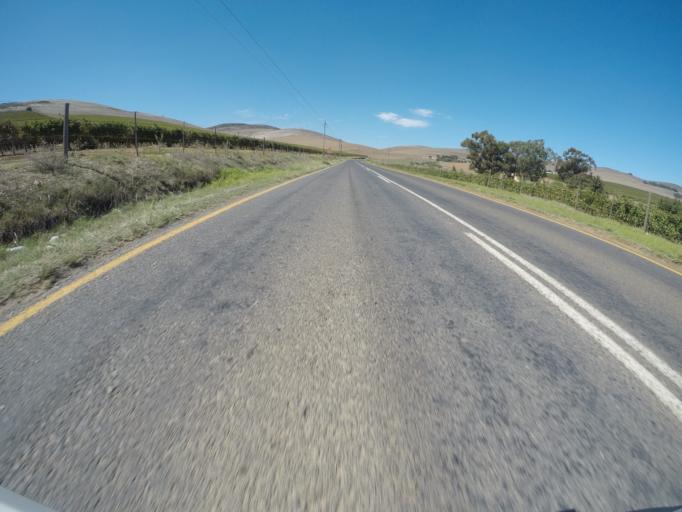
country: ZA
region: Western Cape
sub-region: City of Cape Town
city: Sunset Beach
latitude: -33.7886
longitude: 18.5938
